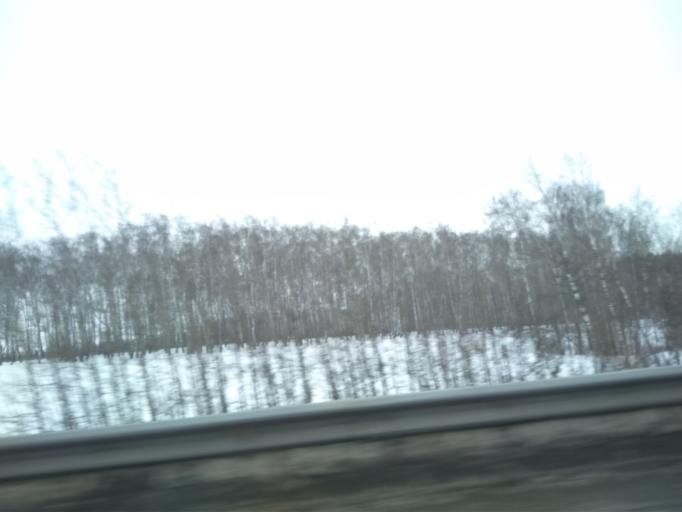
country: RU
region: Moskovskaya
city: Vostryakovo
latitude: 55.4688
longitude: 37.8537
